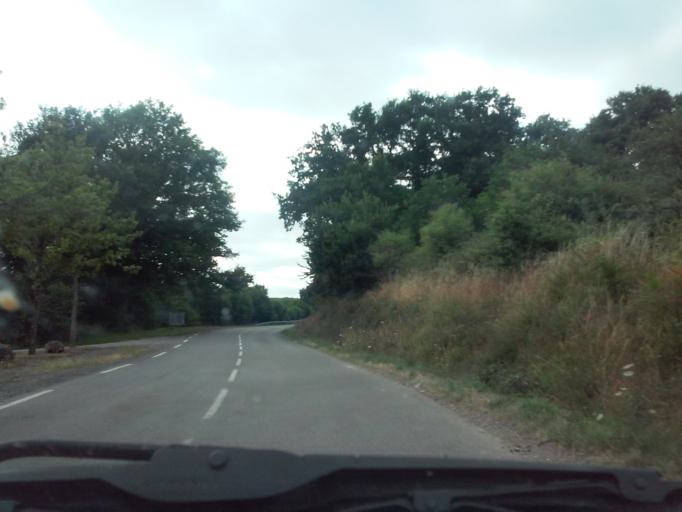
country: FR
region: Brittany
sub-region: Departement d'Ille-et-Vilaine
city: Saint-Senoux
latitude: 47.9076
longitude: -1.7896
